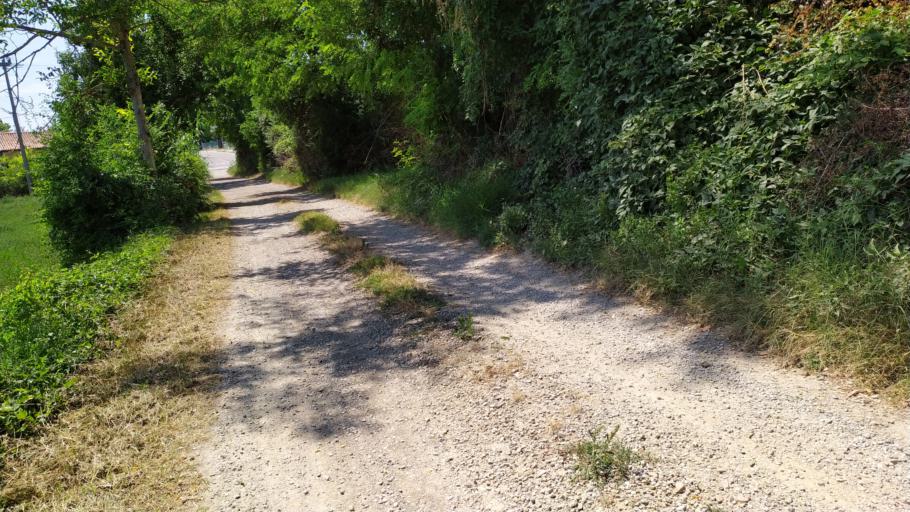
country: IT
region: Emilia-Romagna
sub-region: Forli-Cesena
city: Castrocaro Terme e Terra del Sole
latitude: 44.1873
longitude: 11.9643
